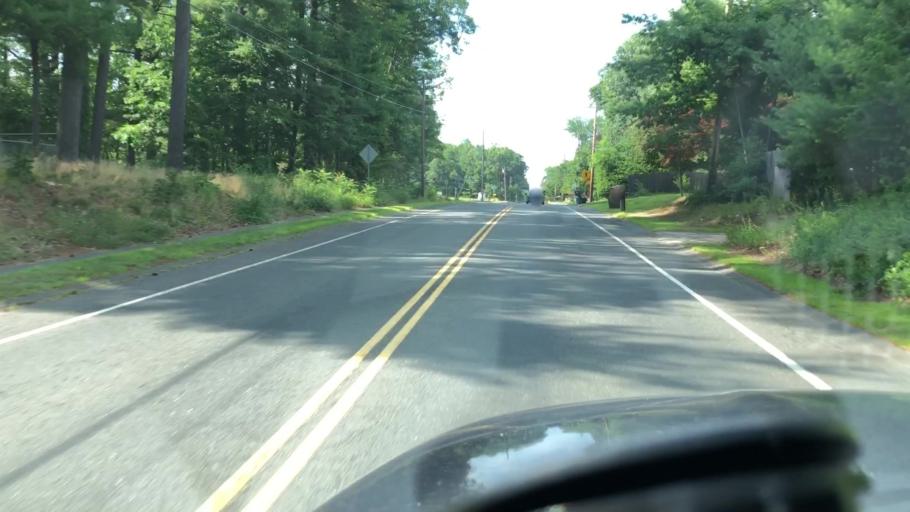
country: US
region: Massachusetts
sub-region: Hampshire County
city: Southampton
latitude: 42.2010
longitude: -72.6884
